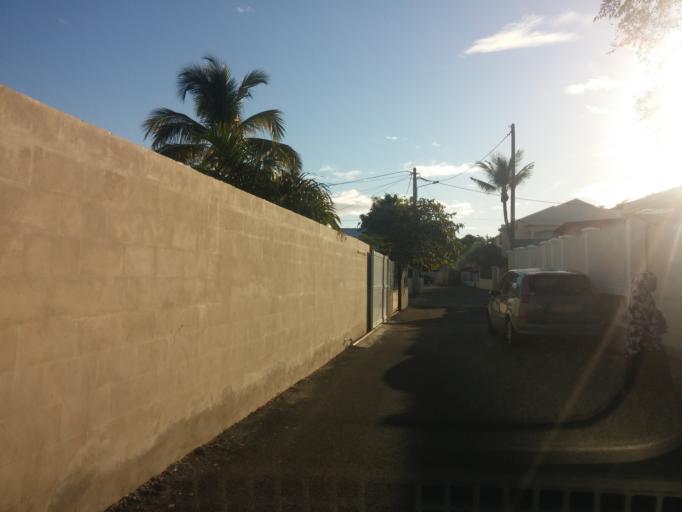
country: RE
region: Reunion
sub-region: Reunion
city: Le Port
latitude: -20.9353
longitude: 55.2941
